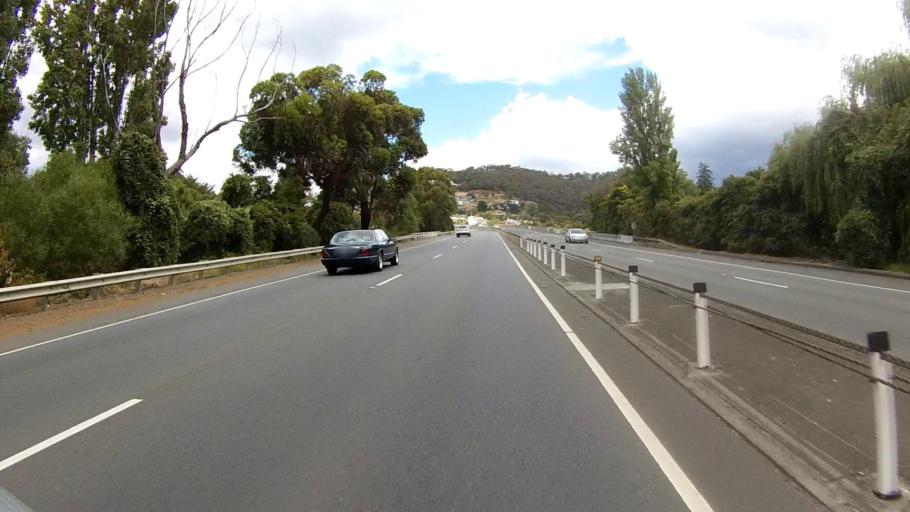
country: AU
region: Tasmania
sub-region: Hobart
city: Dynnyrne
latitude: -42.8975
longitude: 147.3166
